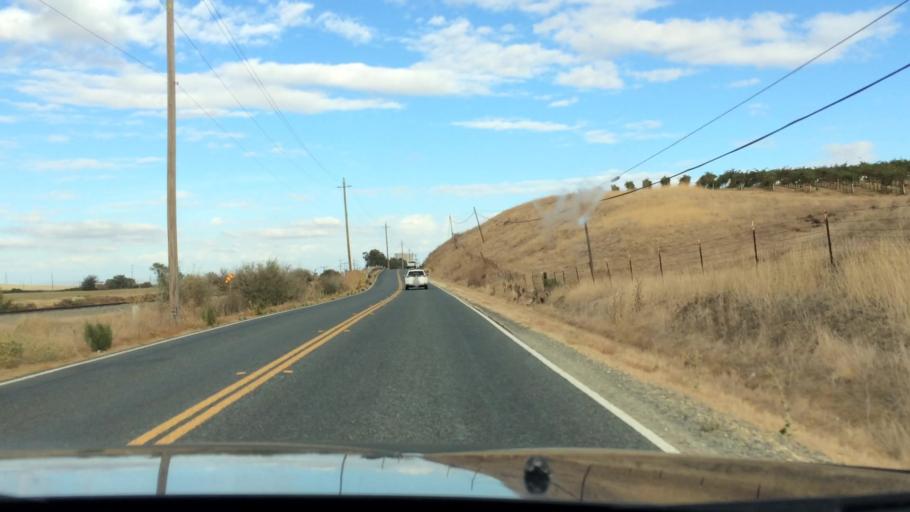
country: US
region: California
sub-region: Sacramento County
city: Clay
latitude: 38.3335
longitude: -121.1747
